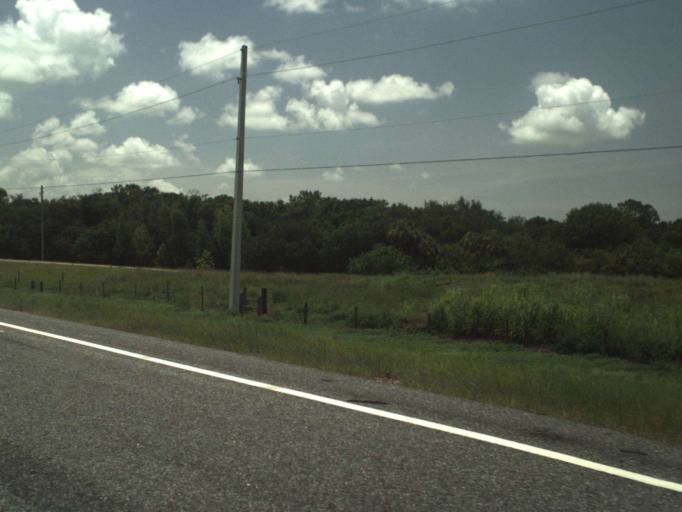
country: US
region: Florida
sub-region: Saint Lucie County
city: Fort Pierce South
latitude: 27.3698
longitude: -80.5595
